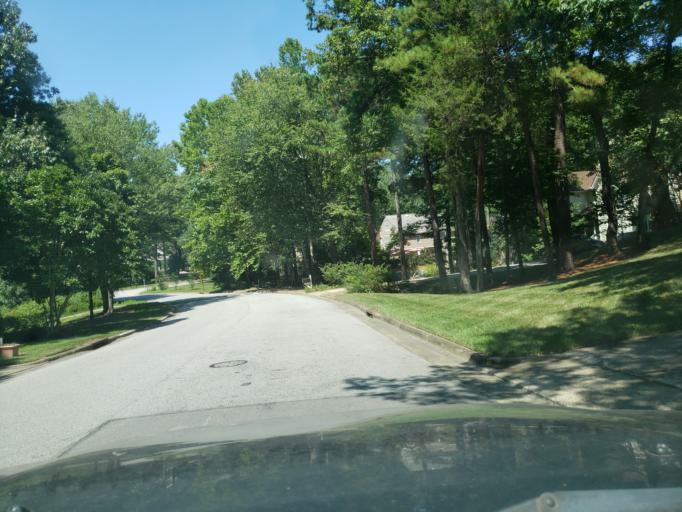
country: US
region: North Carolina
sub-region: Durham County
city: Durham
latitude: 35.9175
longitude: -78.9435
